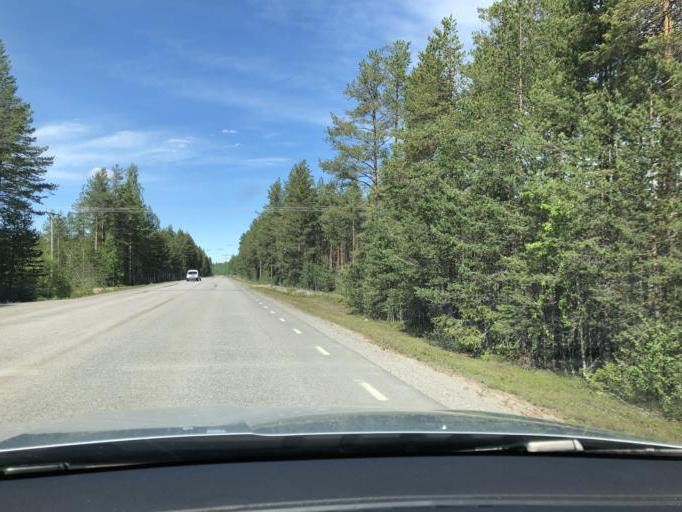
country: SE
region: Norrbotten
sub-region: Pitea Kommun
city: Bergsviken
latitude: 65.3768
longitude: 21.3467
